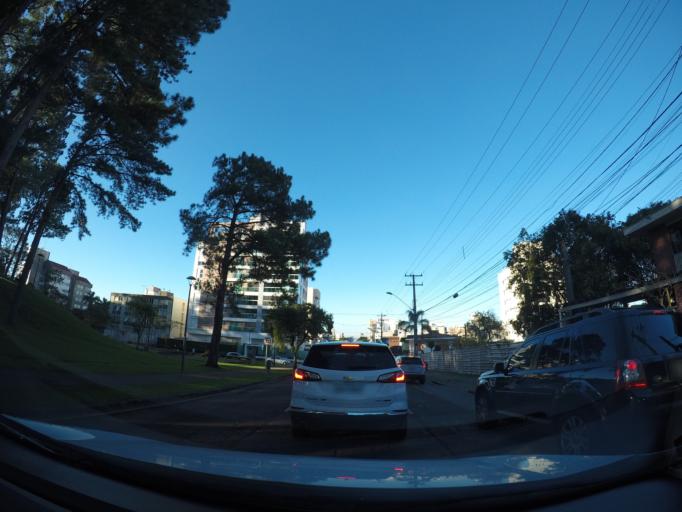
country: BR
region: Parana
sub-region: Curitiba
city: Curitiba
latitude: -25.4152
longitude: -49.2538
